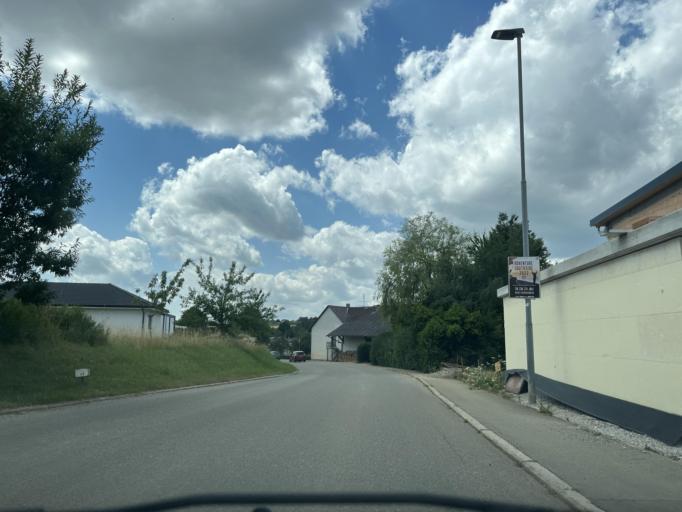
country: DE
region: Baden-Wuerttemberg
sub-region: Tuebingen Region
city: Leibertingen
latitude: 48.0413
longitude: 9.0161
